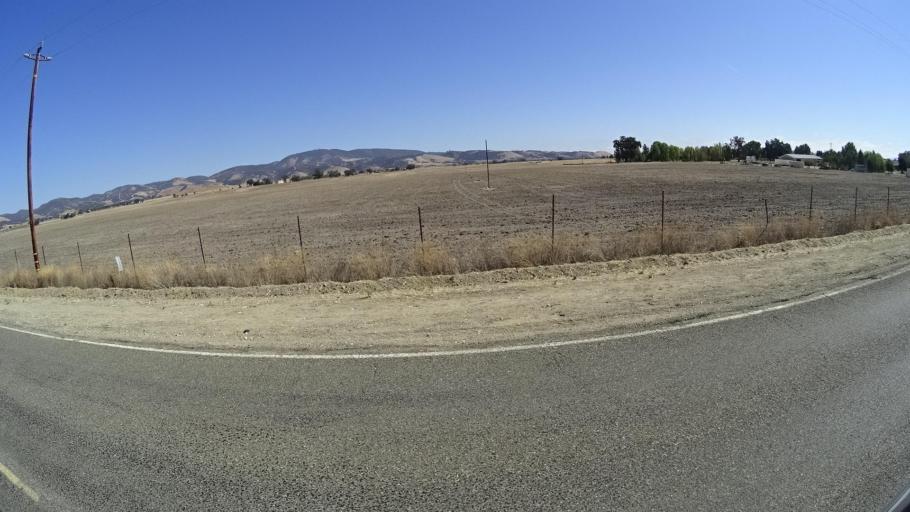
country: US
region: California
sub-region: Monterey County
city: King City
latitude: 35.9304
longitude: -121.0827
